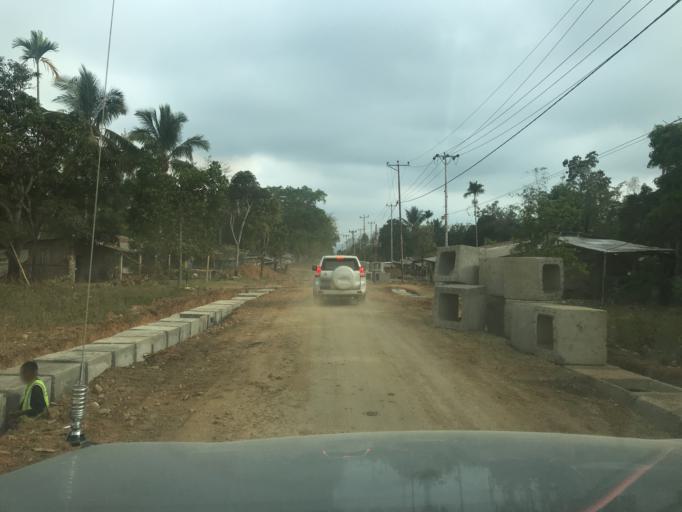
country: TL
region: Ainaro
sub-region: Ainaro
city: Ainaro
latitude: -9.0056
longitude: 125.5018
